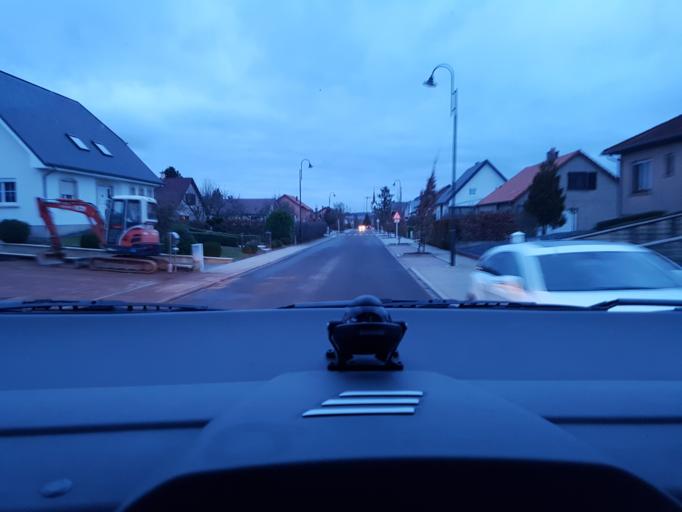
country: LU
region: Grevenmacher
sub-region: Canton de Remich
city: Mondorf-les-Bains
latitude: 49.5031
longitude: 6.3204
